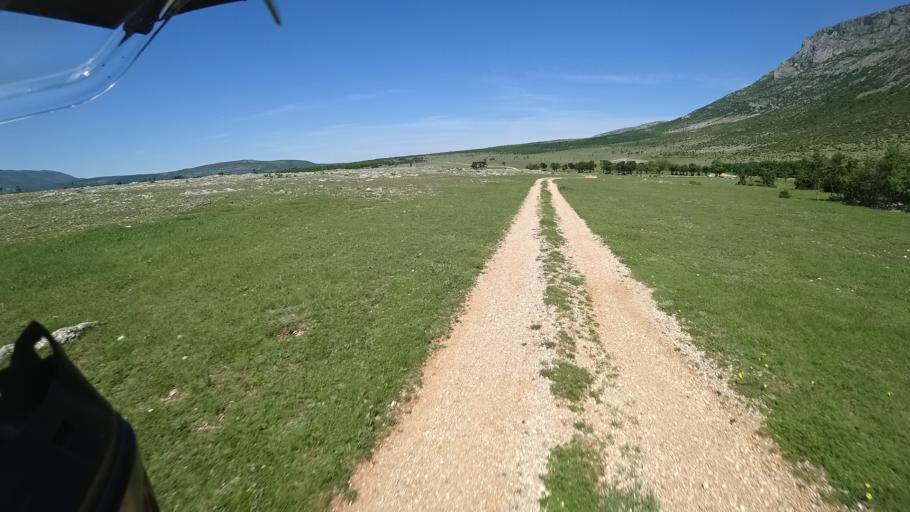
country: BA
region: Federation of Bosnia and Herzegovina
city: Bosansko Grahovo
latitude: 44.0021
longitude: 16.4017
